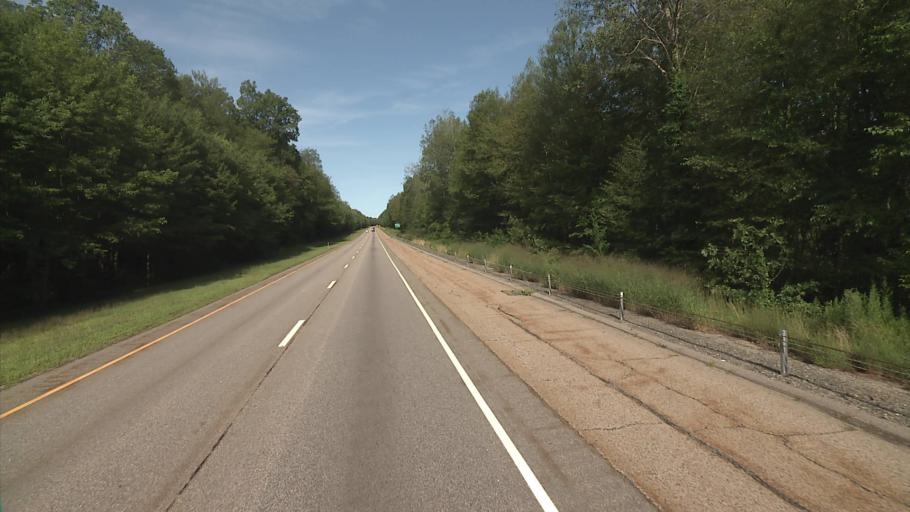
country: US
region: Connecticut
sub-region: New London County
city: Colchester
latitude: 41.5689
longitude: -72.2699
